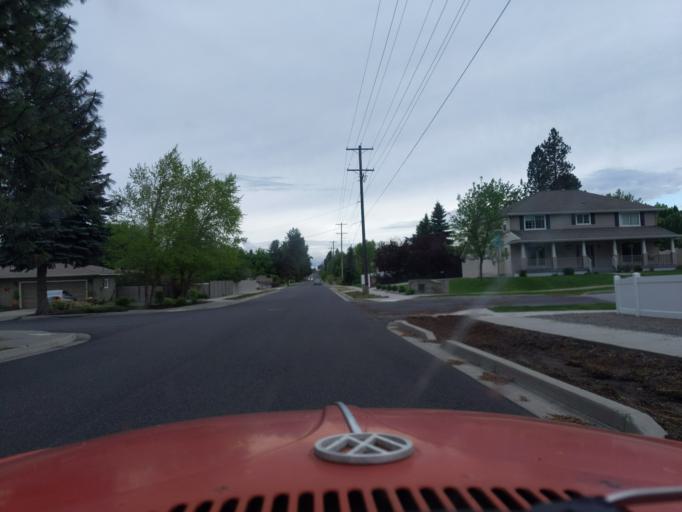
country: US
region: Washington
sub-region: Spokane County
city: Spokane
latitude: 47.6114
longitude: -117.3790
